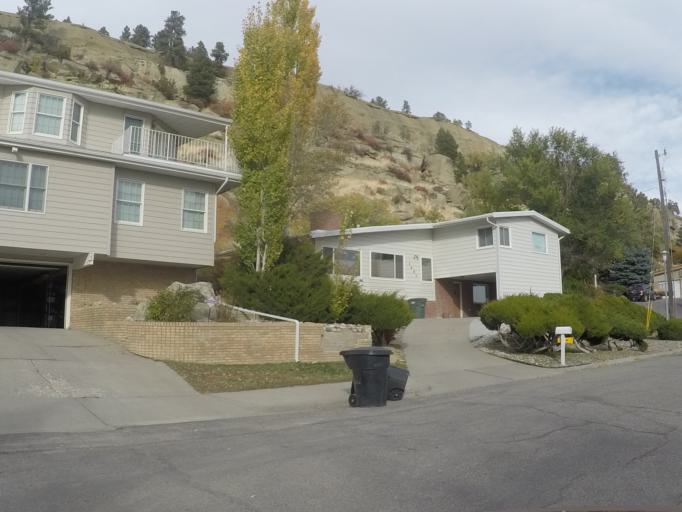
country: US
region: Montana
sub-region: Yellowstone County
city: Billings
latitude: 45.8010
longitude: -108.5539
